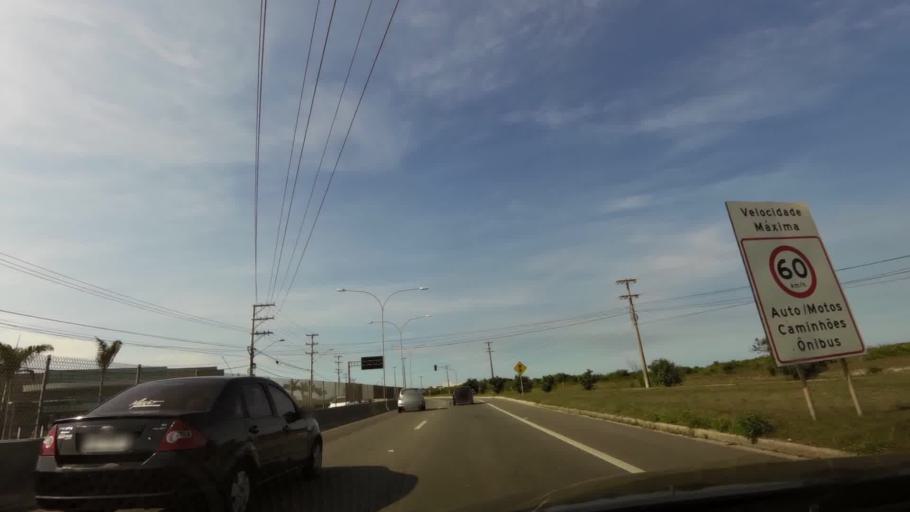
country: BR
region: Espirito Santo
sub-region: Vila Velha
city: Vila Velha
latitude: -20.3940
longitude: -40.3178
